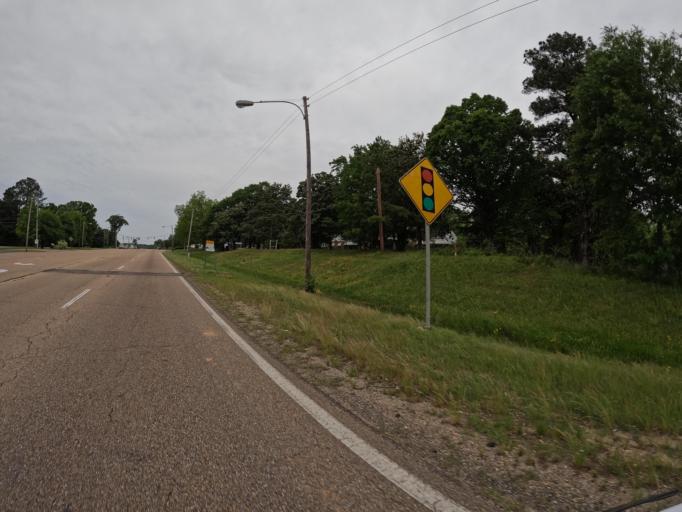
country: US
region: Mississippi
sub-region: Lee County
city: Tupelo
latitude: 34.2842
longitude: -88.7361
